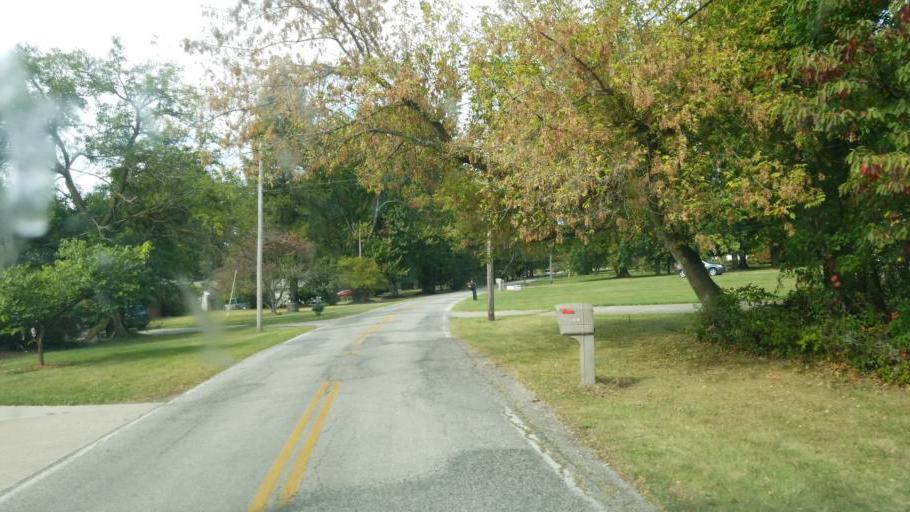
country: US
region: Ohio
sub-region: Lorain County
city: Vermilion-on-the-Lake
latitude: 41.3896
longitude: -82.2958
